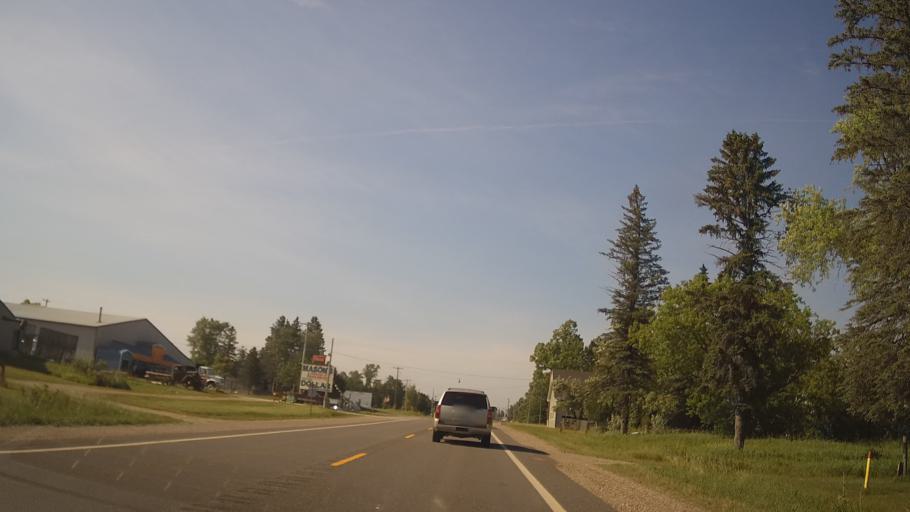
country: US
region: Michigan
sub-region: Ogemaw County
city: West Branch
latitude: 44.4058
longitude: -84.1164
